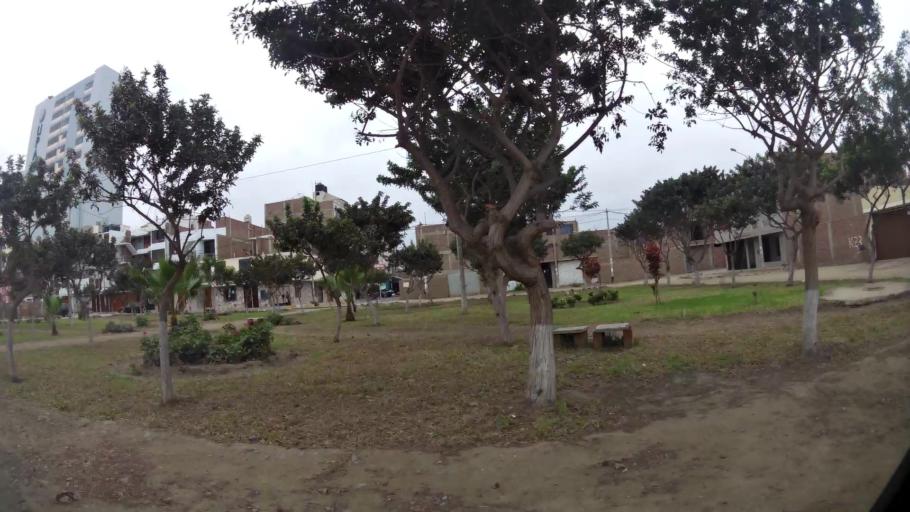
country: PE
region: La Libertad
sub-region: Provincia de Trujillo
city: Trujillo
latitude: -8.1155
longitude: -79.0465
